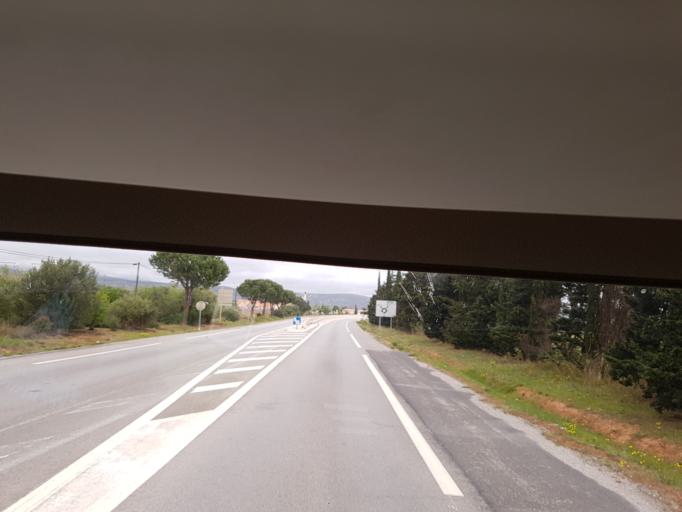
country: FR
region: Languedoc-Roussillon
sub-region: Departement des Pyrenees-Orientales
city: Salses-le-Chateau
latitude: 42.8203
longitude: 2.9161
